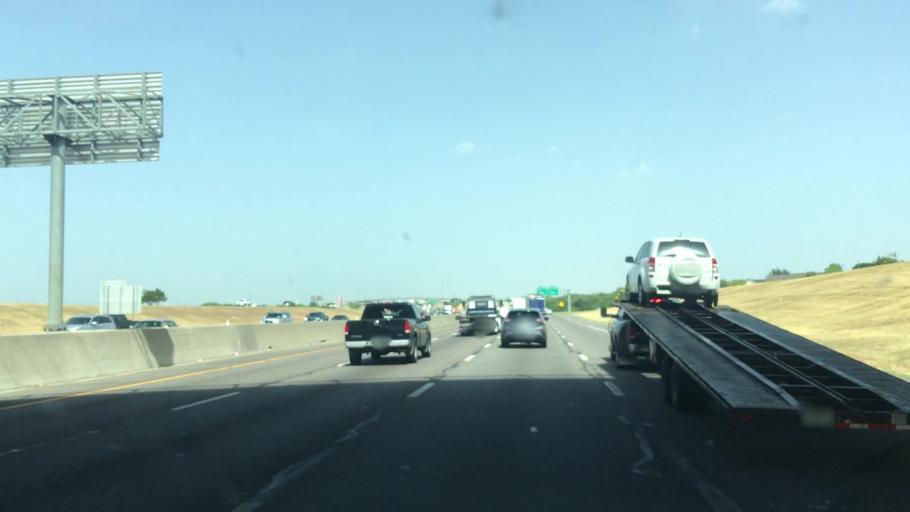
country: US
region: Texas
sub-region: Dallas County
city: DeSoto
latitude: 32.6427
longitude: -96.8399
